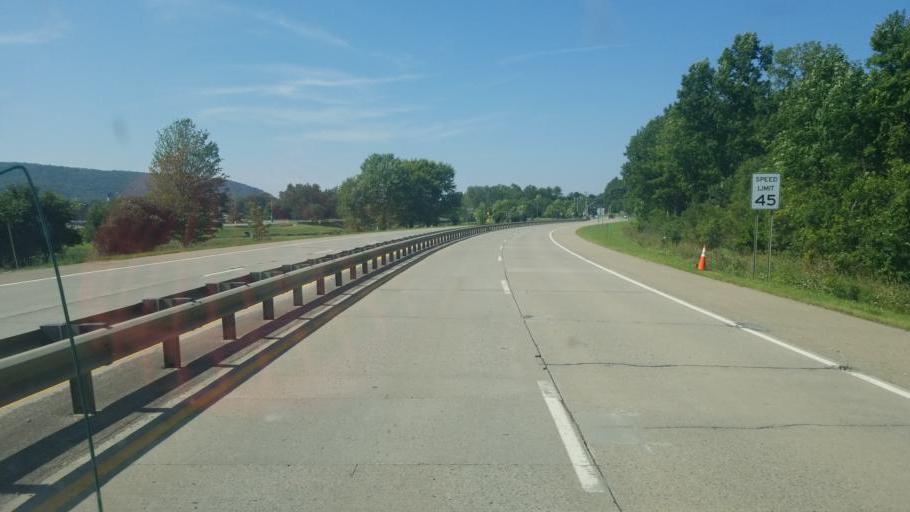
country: US
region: New York
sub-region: Allegany County
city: Wellsville
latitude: 42.1254
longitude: -77.9582
